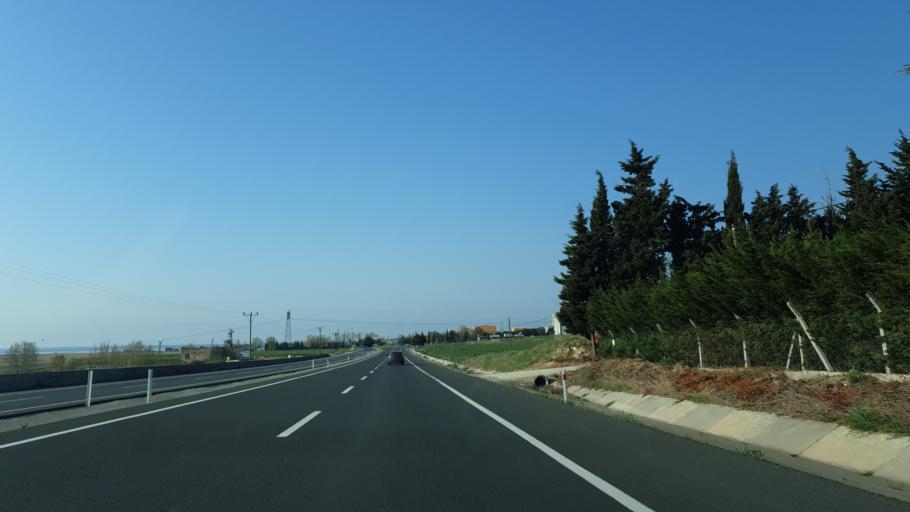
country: TR
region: Tekirdag
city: Corlu
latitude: 41.0280
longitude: 27.7255
